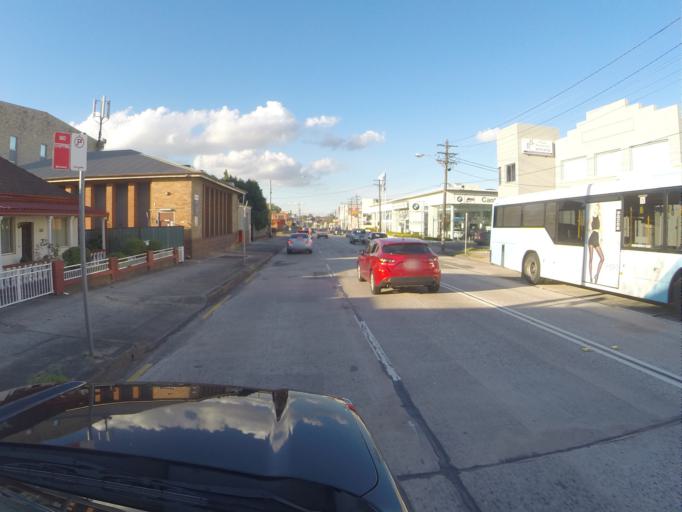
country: AU
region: New South Wales
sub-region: Canterbury
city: Canterbury
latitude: -33.9161
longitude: 151.1092
